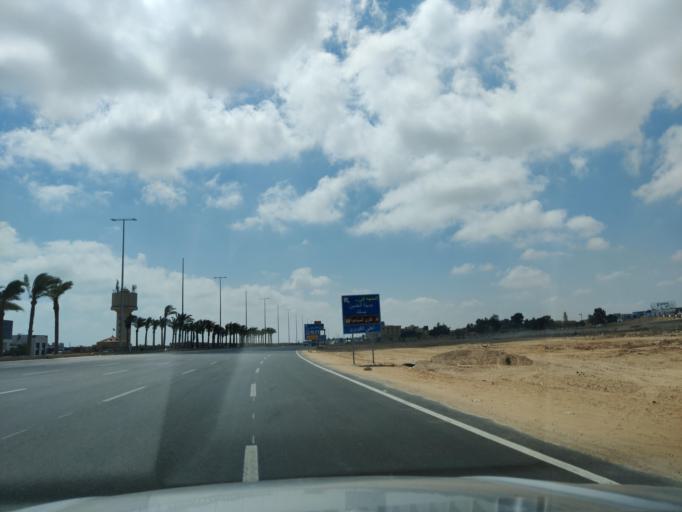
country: EG
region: Muhafazat Matruh
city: Al `Alamayn
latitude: 30.8444
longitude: 28.9433
